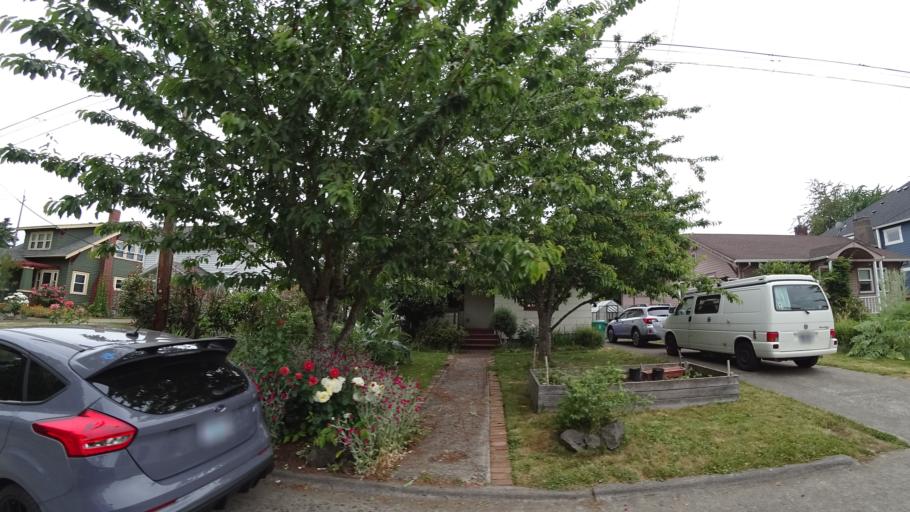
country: US
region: Oregon
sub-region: Multnomah County
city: Portland
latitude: 45.5710
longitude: -122.6915
